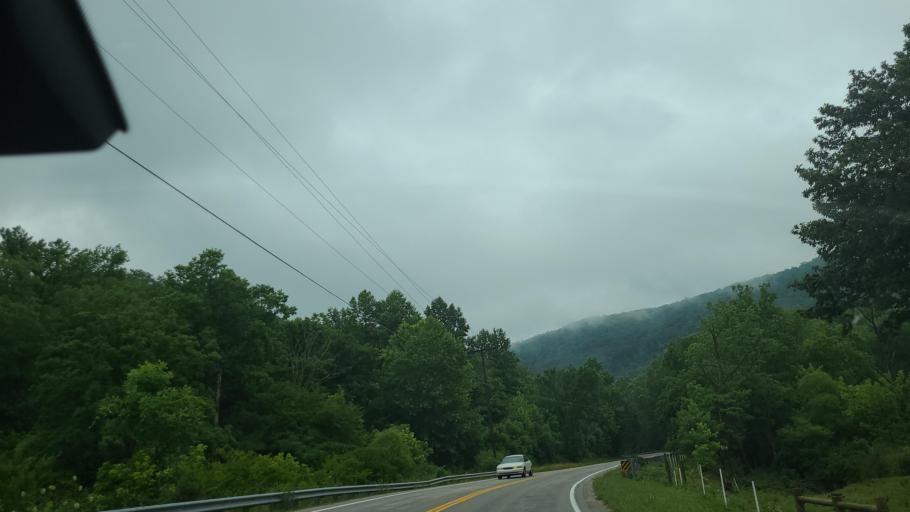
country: US
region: Tennessee
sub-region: Anderson County
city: Oak Ridge
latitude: 36.0919
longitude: -84.2724
